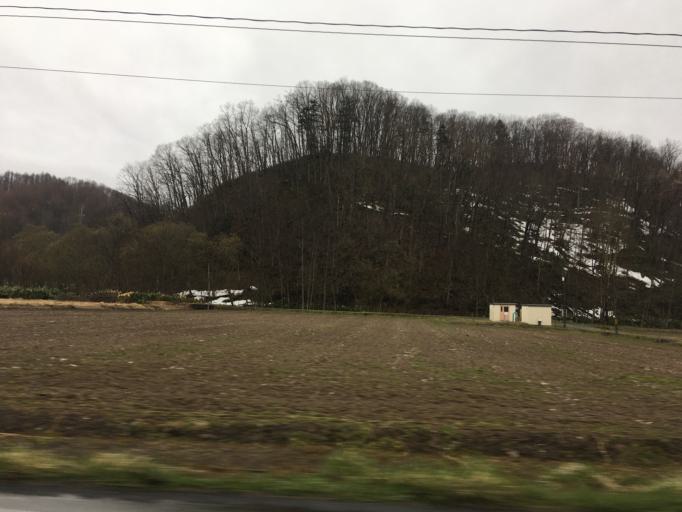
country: JP
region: Hokkaido
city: Nayoro
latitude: 44.0888
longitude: 142.4493
